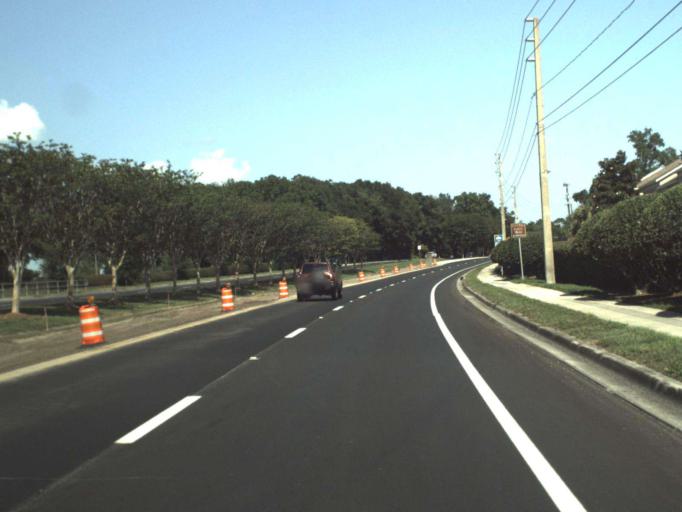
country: US
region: Florida
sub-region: Seminole County
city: Winter Springs
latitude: 28.7052
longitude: -81.2727
